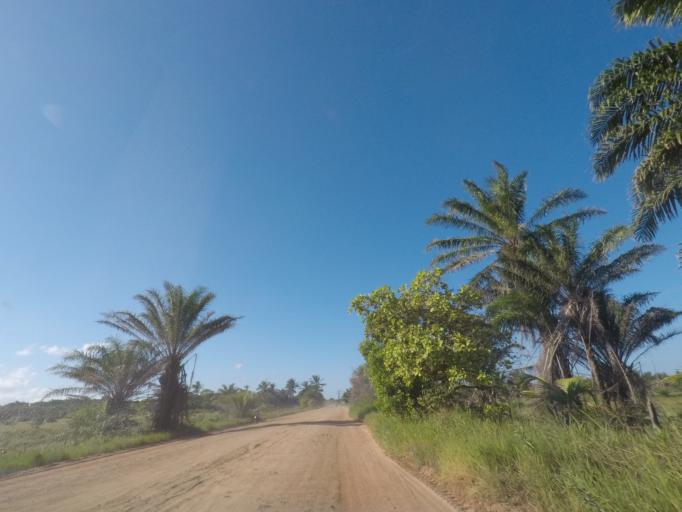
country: BR
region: Bahia
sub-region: Marau
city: Marau
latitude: -14.0471
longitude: -38.9546
